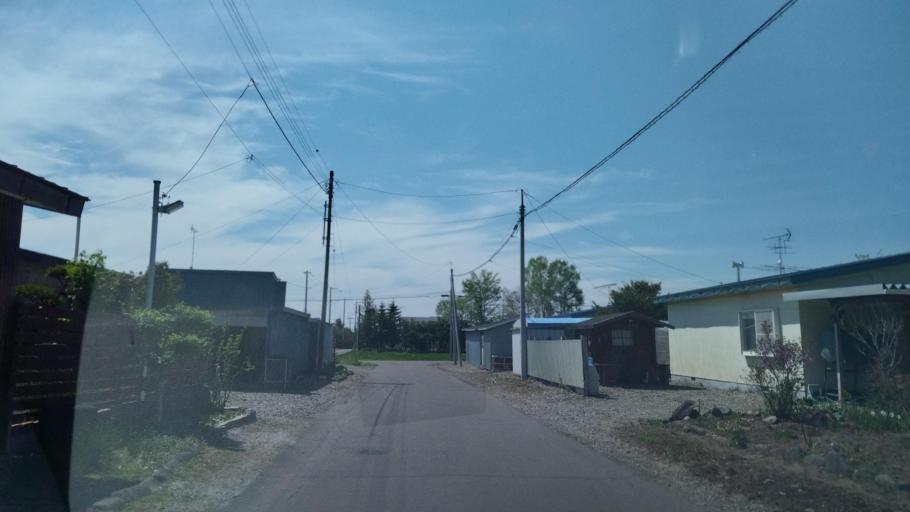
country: JP
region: Hokkaido
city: Otofuke
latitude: 43.2393
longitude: 143.2911
